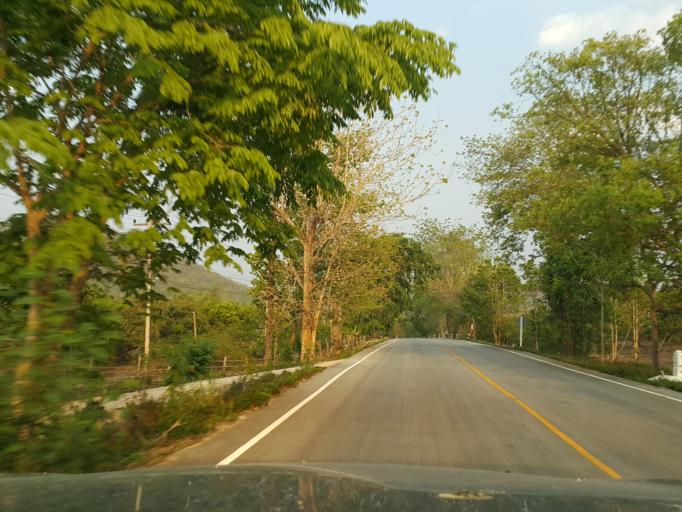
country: TH
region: Lamphun
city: Li
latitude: 17.8455
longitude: 98.9995
